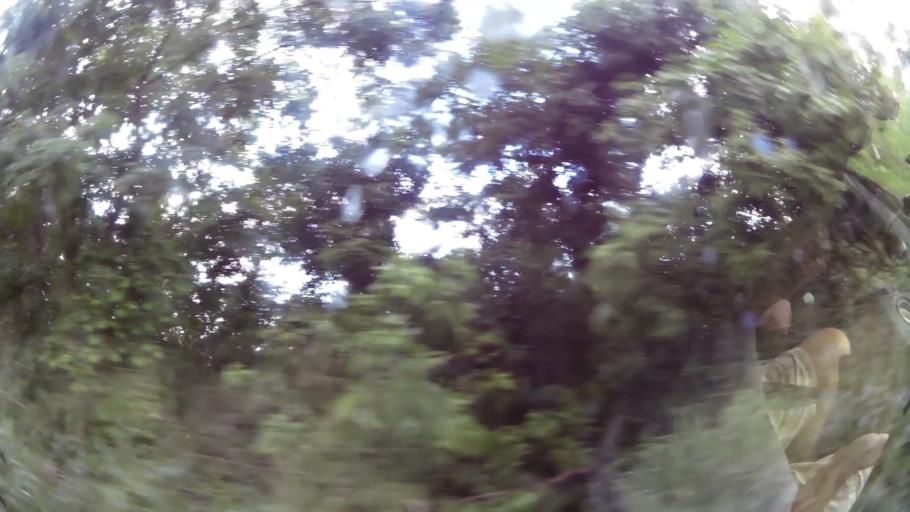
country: DM
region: Saint George
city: Roseau
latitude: 15.3285
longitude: -61.3923
